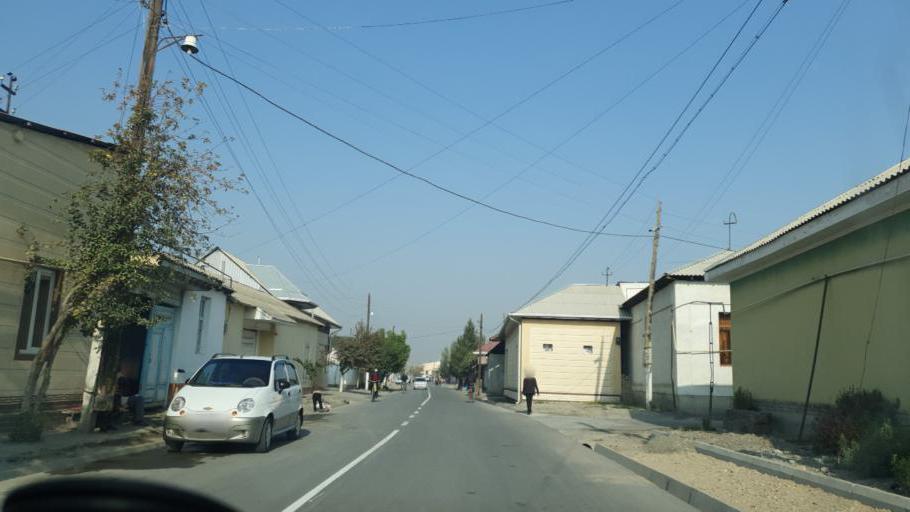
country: UZ
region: Fergana
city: Qo`qon
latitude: 40.5806
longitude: 70.9126
